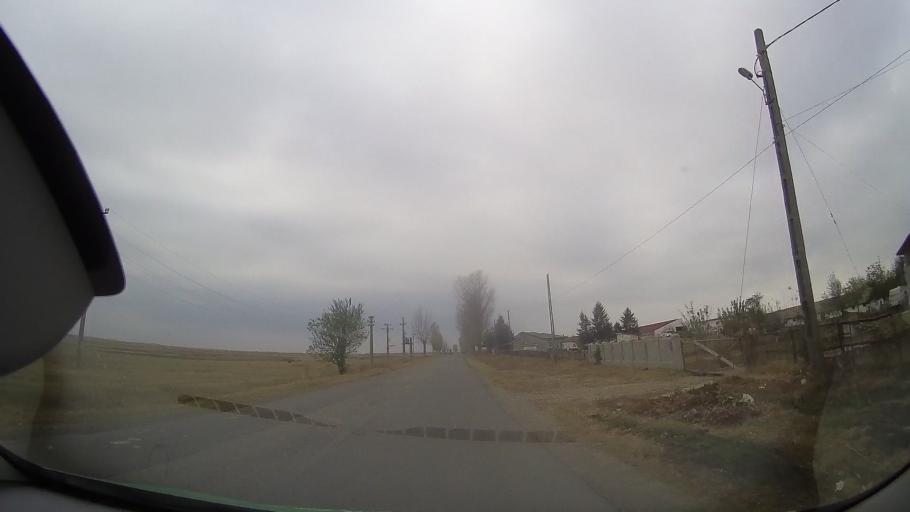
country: RO
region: Buzau
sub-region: Comuna Pogoanele
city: Pogoanele
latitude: 44.9012
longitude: 26.9765
